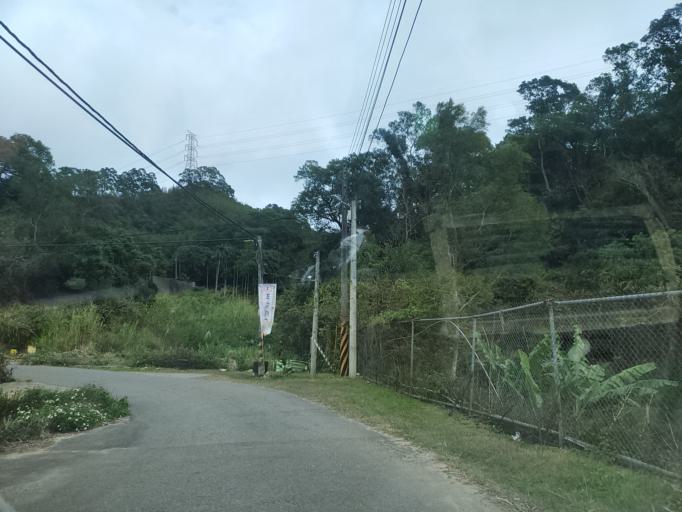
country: TW
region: Taiwan
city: Fengyuan
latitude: 24.3548
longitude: 120.7759
